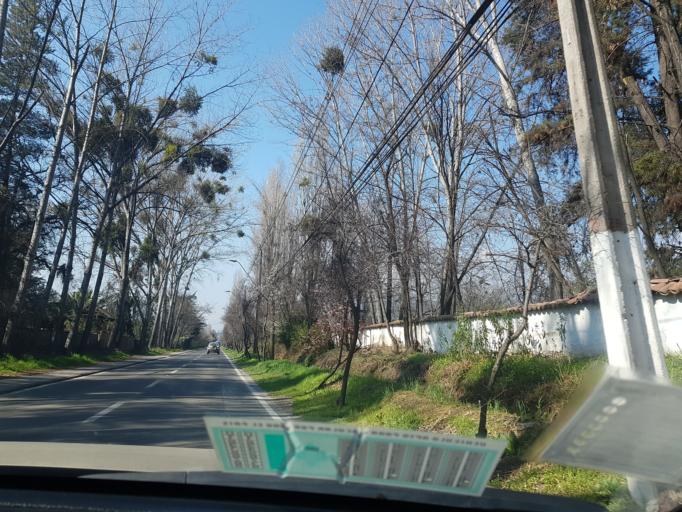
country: CL
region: Santiago Metropolitan
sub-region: Provincia de Cordillera
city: Puente Alto
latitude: -33.6322
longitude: -70.5643
